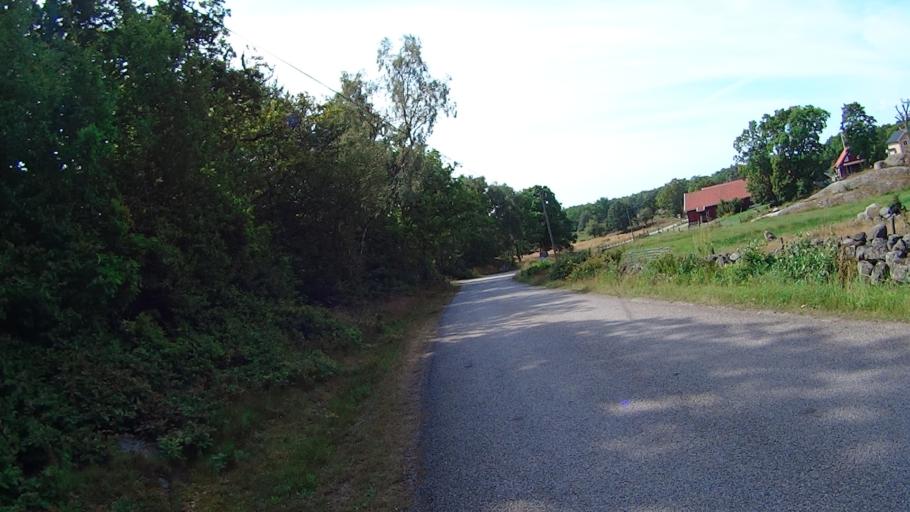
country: SE
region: Blekinge
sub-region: Ronneby Kommun
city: Brakne-Hoby
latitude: 56.1594
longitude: 15.0885
